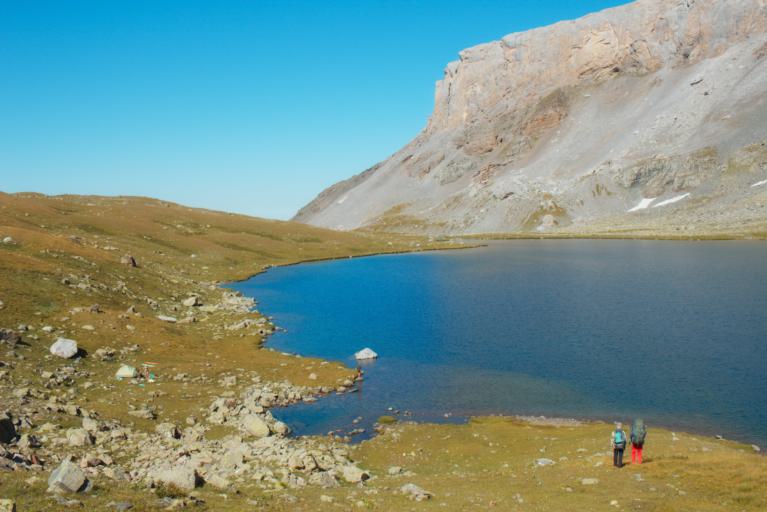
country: RU
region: Karachayevo-Cherkesiya
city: Nizhniy Arkhyz
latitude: 43.5955
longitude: 41.1932
